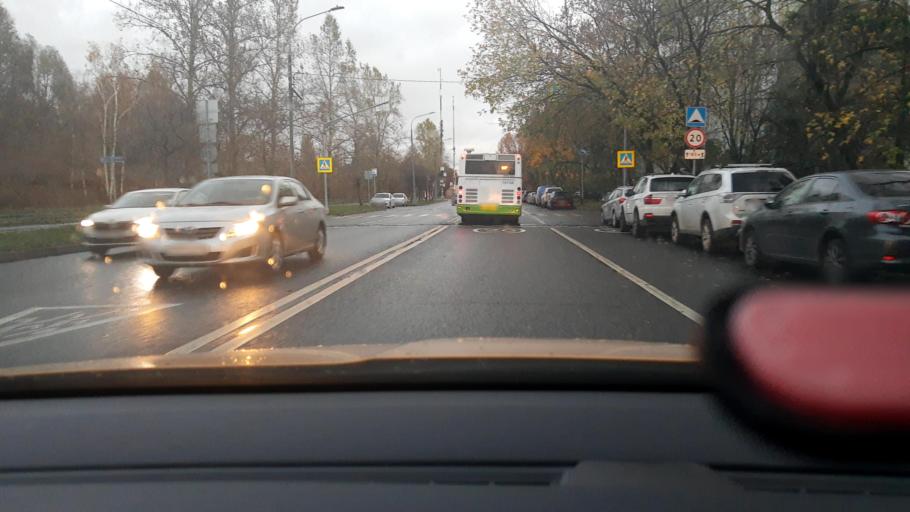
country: RU
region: Moscow
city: Strogino
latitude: 55.8144
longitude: 37.4081
